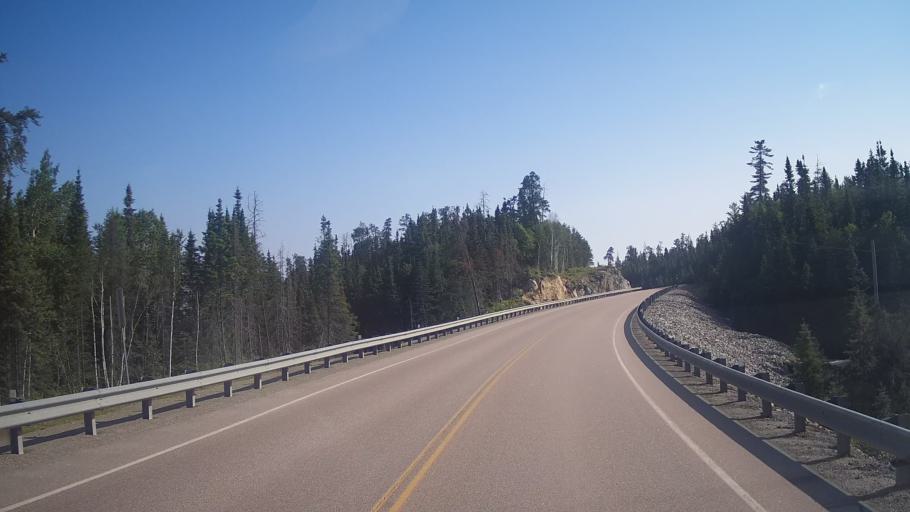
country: CA
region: Ontario
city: Rayside-Balfour
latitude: 47.0254
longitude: -81.6392
